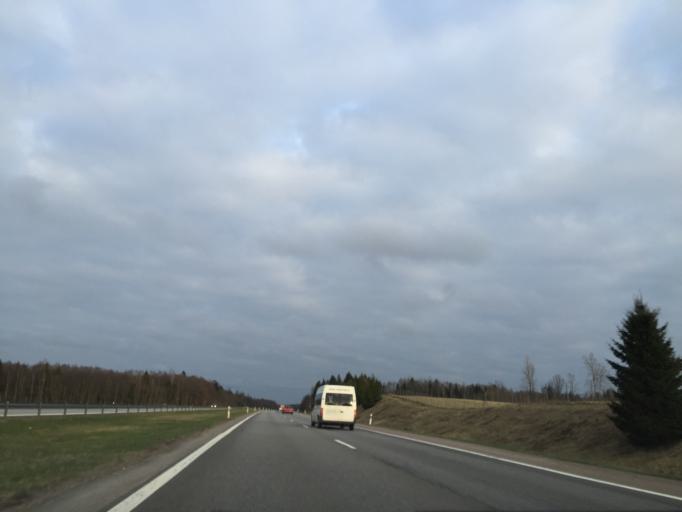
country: LT
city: Rietavas
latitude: 55.6585
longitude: 21.7706
